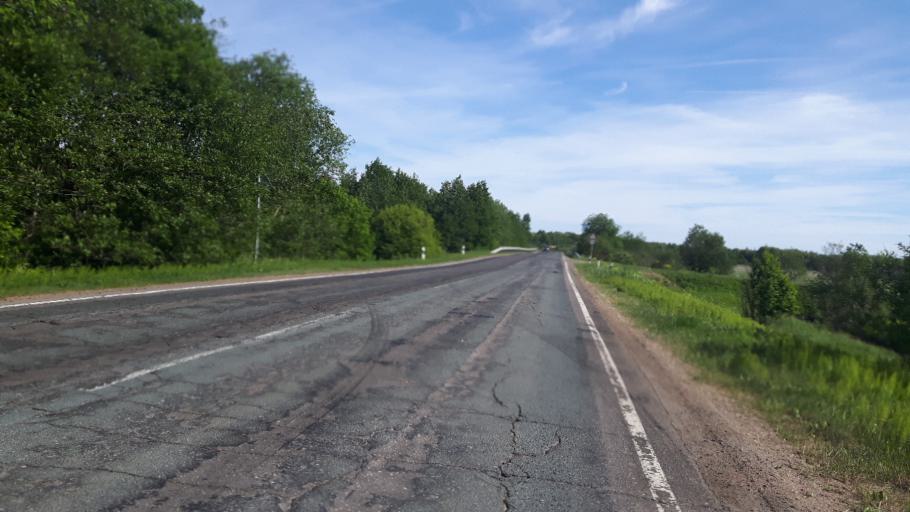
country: RU
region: Leningrad
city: Ivangorod
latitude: 59.4176
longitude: 28.3244
